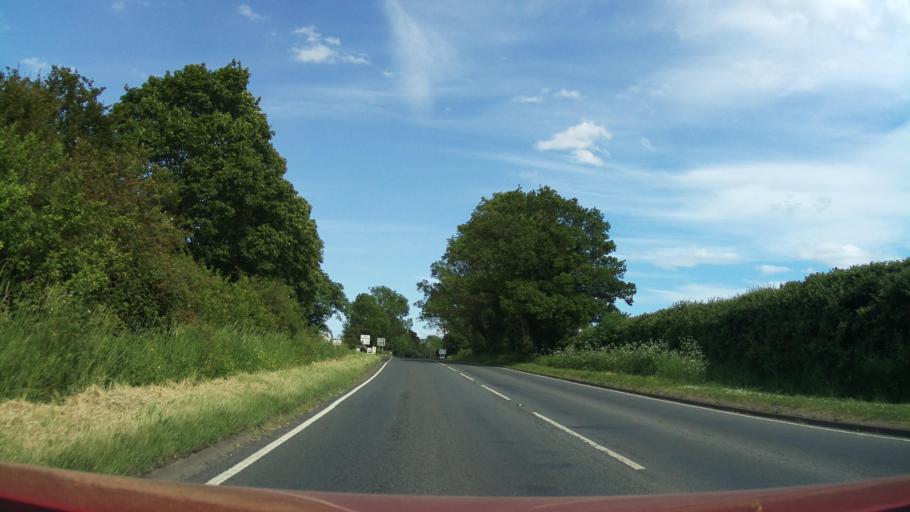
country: GB
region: England
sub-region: Worcestershire
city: Pershore
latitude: 52.1394
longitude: -2.1290
